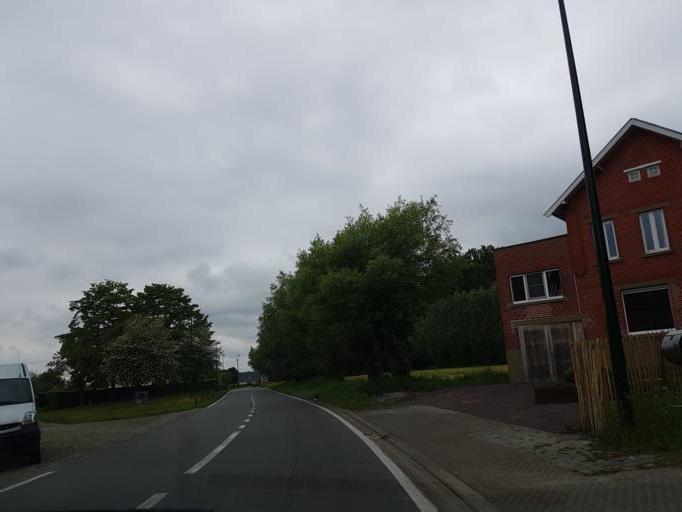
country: BE
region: Flanders
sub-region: Provincie Oost-Vlaanderen
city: Zomergem
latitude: 51.1161
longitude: 3.5538
